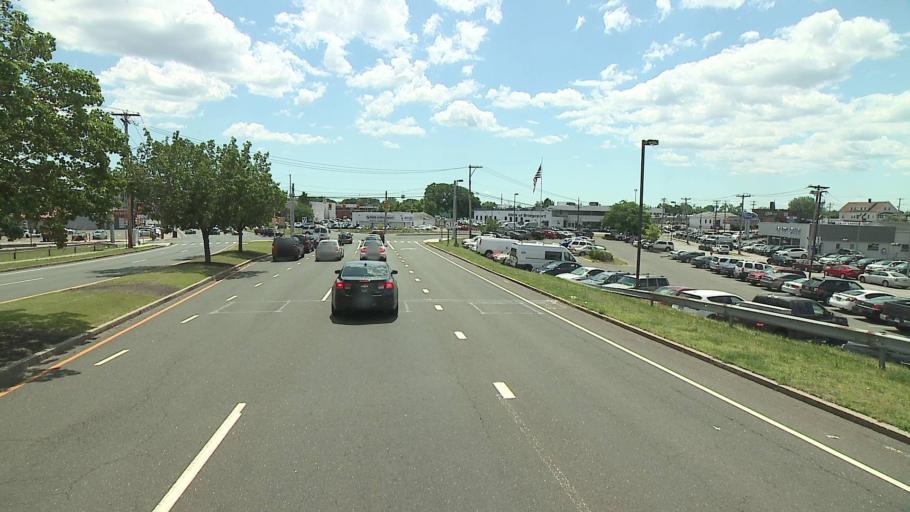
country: US
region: Connecticut
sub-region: Fairfield County
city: Bridgeport
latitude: 41.2037
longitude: -73.1894
